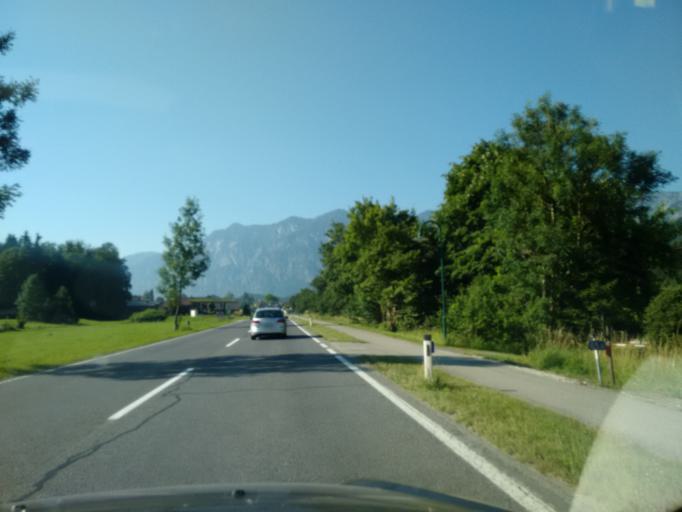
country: AT
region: Upper Austria
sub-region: Politischer Bezirk Gmunden
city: Bad Goisern
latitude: 47.6580
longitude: 13.6094
